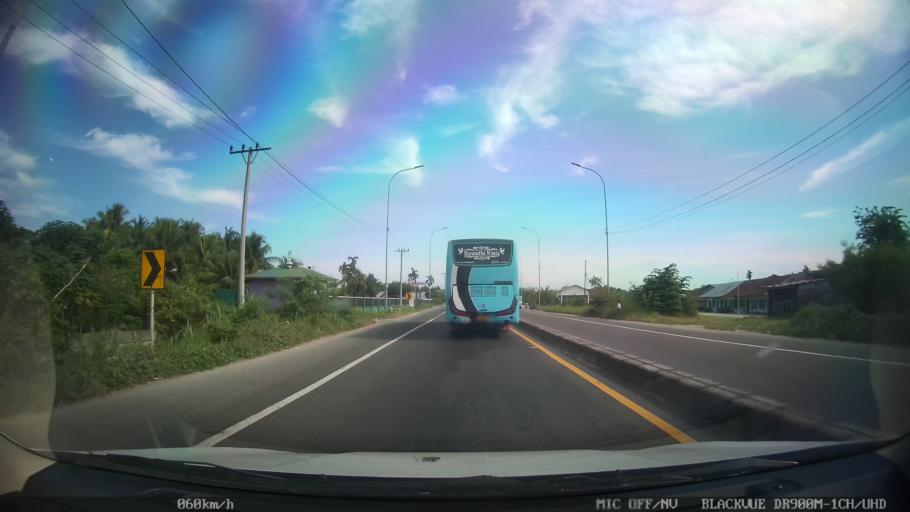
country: ID
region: North Sumatra
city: Sunggal
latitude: 3.6192
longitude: 98.6285
